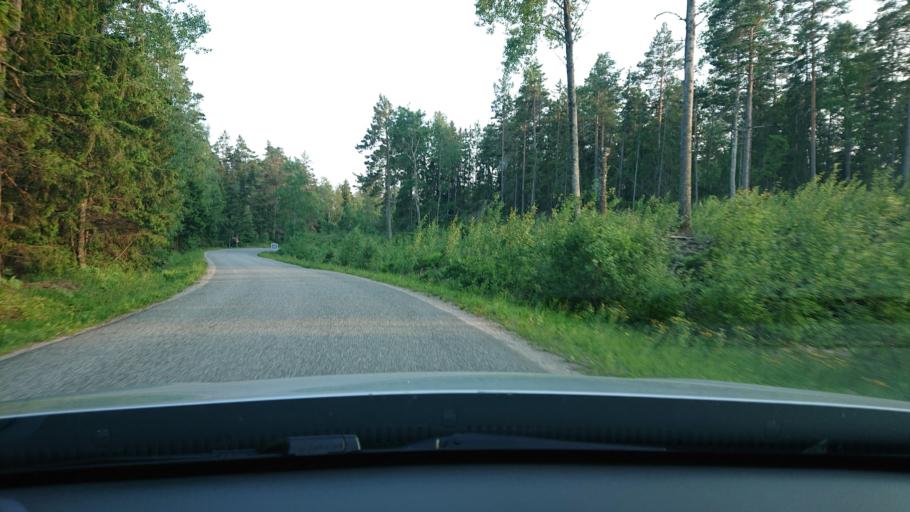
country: SE
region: Stockholm
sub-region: Osterakers Kommun
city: Akersberga
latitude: 59.5192
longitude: 18.3281
